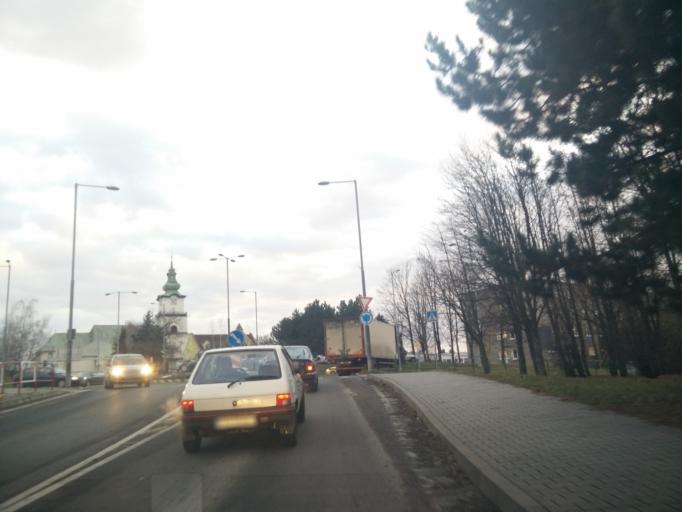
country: SK
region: Nitriansky
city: Prievidza
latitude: 48.7749
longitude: 18.6248
